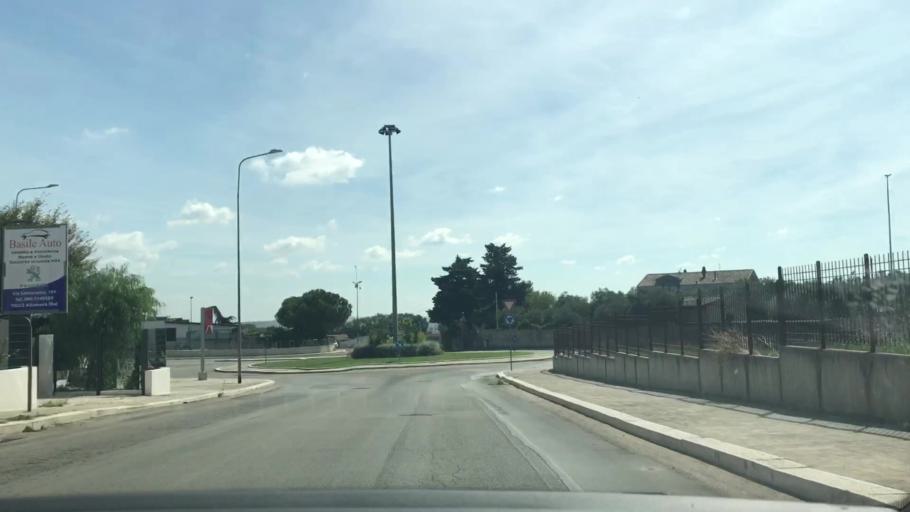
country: IT
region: Apulia
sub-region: Provincia di Bari
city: Altamura
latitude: 40.8255
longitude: 16.5658
